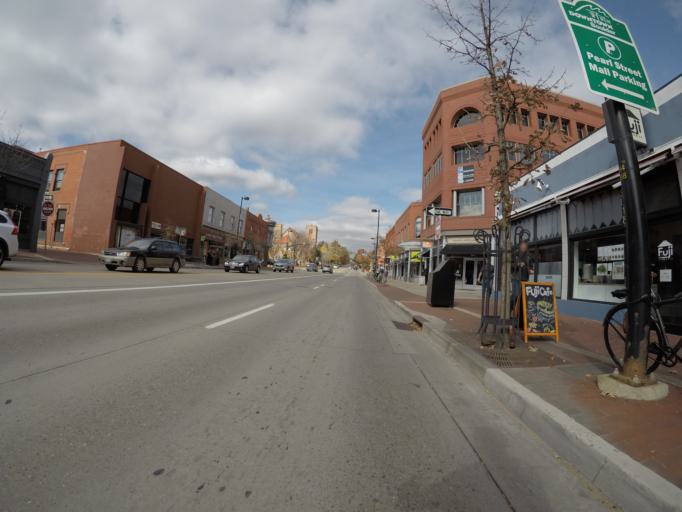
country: US
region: Colorado
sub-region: Boulder County
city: Boulder
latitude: 40.0182
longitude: -105.2799
